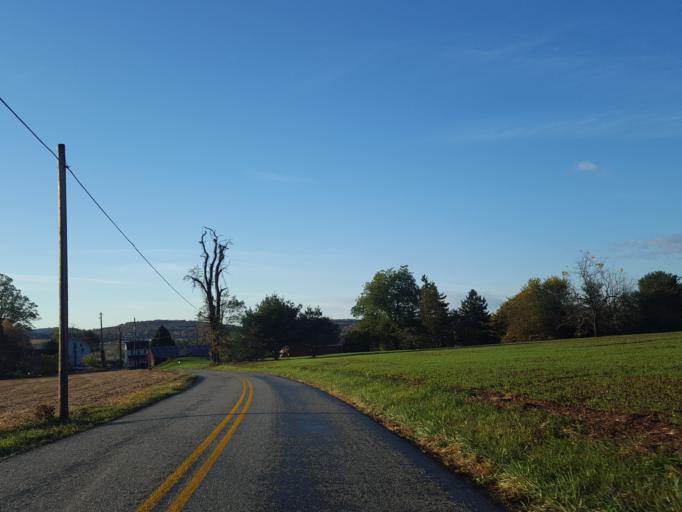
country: US
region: Pennsylvania
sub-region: York County
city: Stonybrook
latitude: 39.9640
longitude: -76.6274
